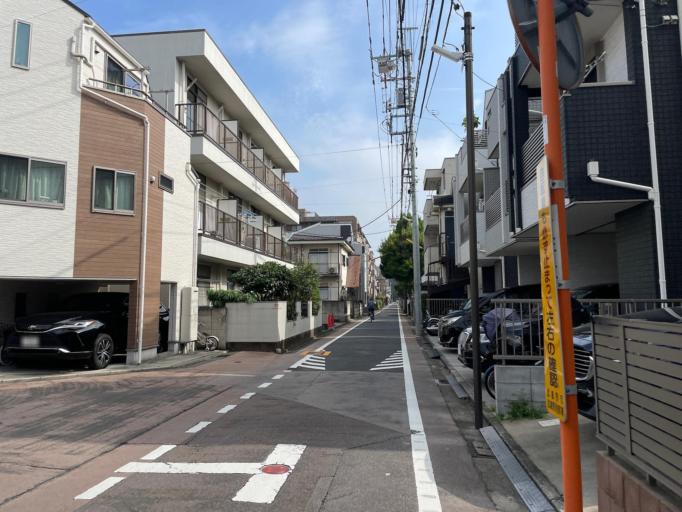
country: JP
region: Tokyo
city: Musashino
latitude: 35.7109
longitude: 139.5582
